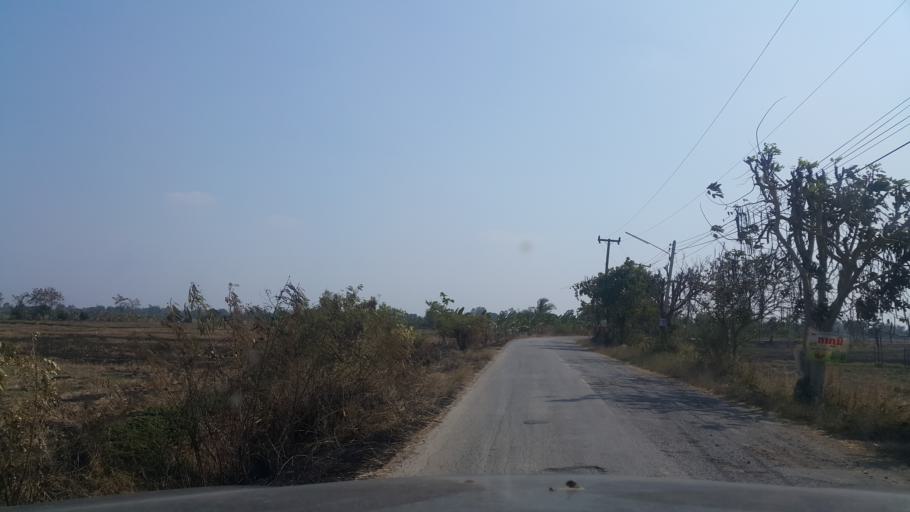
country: TH
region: Nakhon Ratchasima
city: Chok Chai
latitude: 14.6991
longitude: 102.1168
